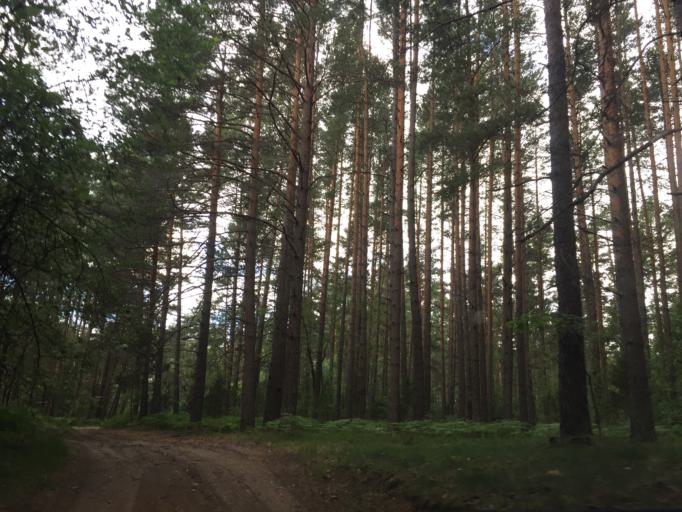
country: LV
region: Adazi
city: Adazi
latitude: 57.1335
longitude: 24.3474
